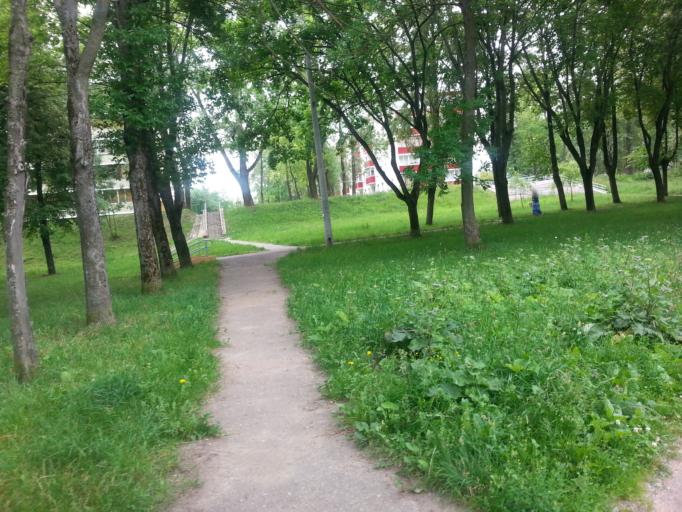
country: BY
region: Minsk
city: Novoye Medvezhino
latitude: 53.9001
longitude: 27.5008
